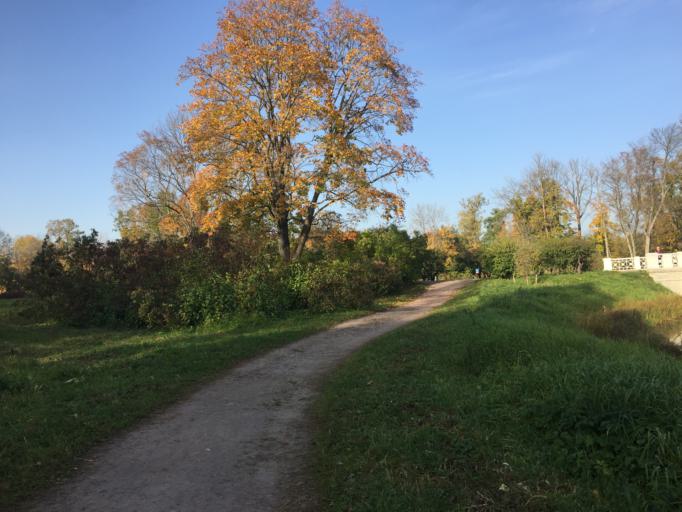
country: RU
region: St.-Petersburg
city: Pushkin
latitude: 59.7222
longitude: 30.3718
